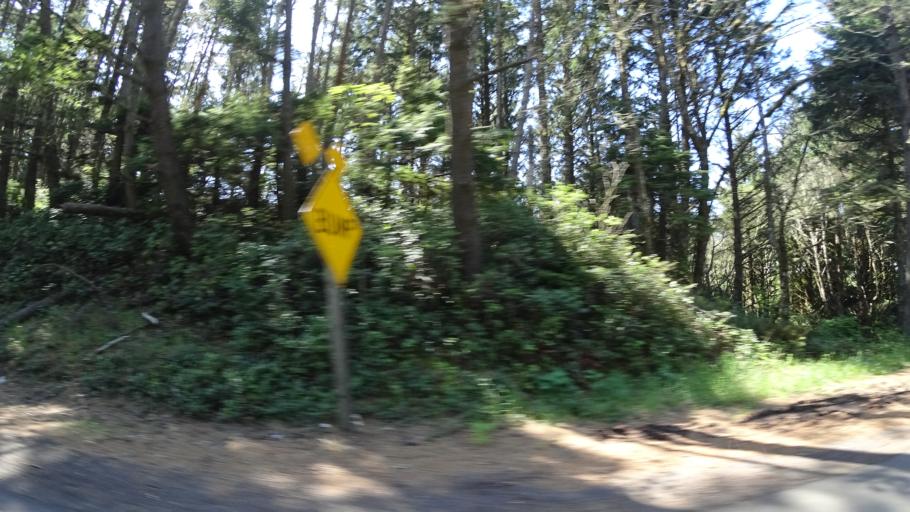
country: US
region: Oregon
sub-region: Lincoln County
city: Depoe Bay
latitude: 44.7413
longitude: -124.0559
